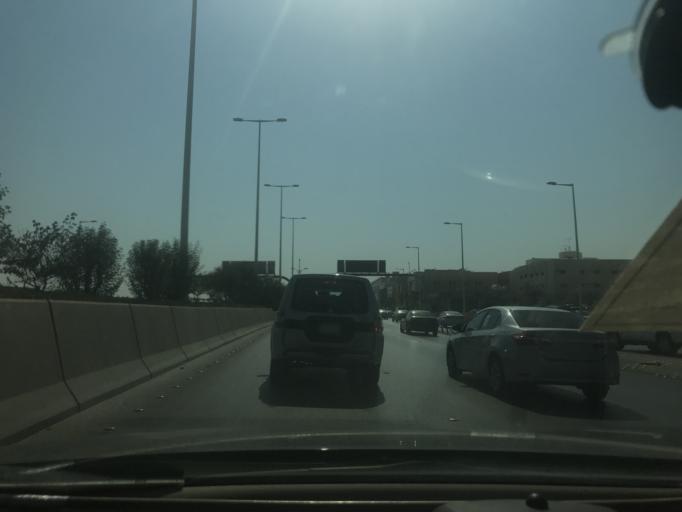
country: SA
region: Ar Riyad
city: Riyadh
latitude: 24.7009
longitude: 46.7229
